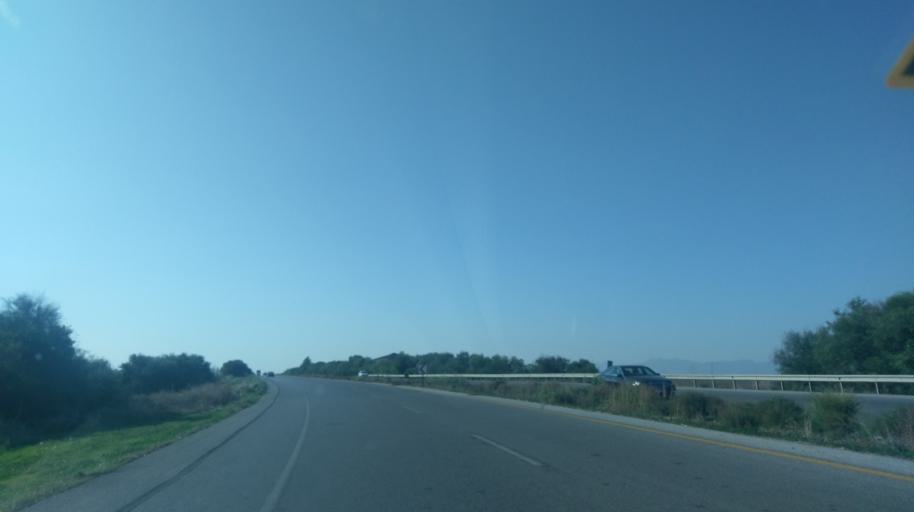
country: CY
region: Ammochostos
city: Acheritou
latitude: 35.1723
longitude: 33.8068
